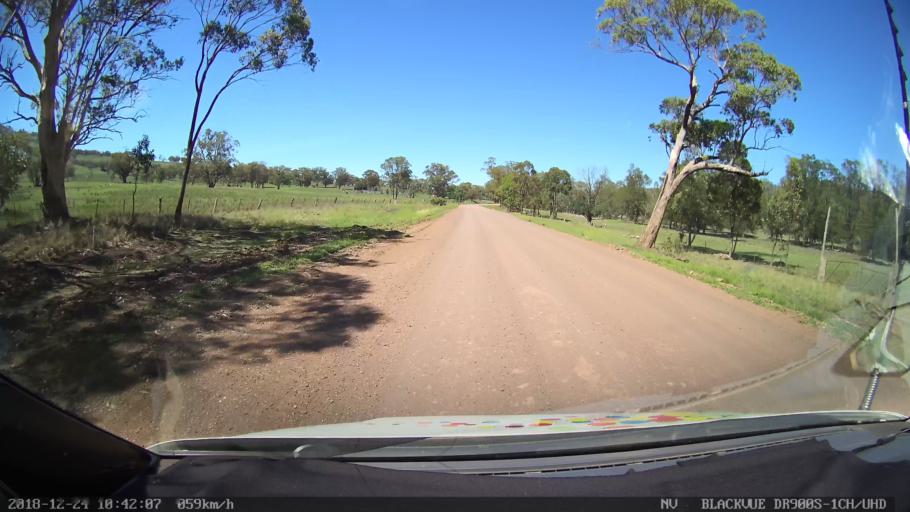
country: AU
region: New South Wales
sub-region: Upper Hunter Shire
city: Merriwa
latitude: -31.8742
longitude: 150.4550
